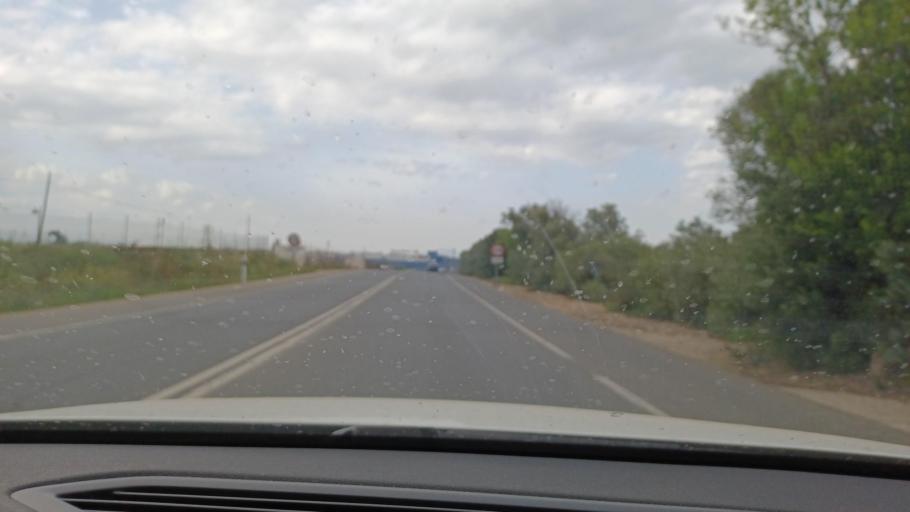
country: ES
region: Valencia
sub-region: Provincia de Castello
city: Vinaros
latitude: 40.4495
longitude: 0.4499
